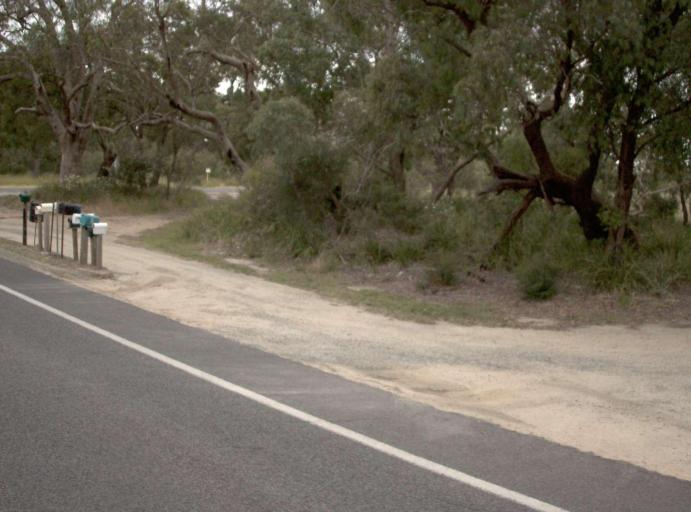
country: AU
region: Victoria
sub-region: Wellington
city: Sale
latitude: -38.1982
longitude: 147.0770
